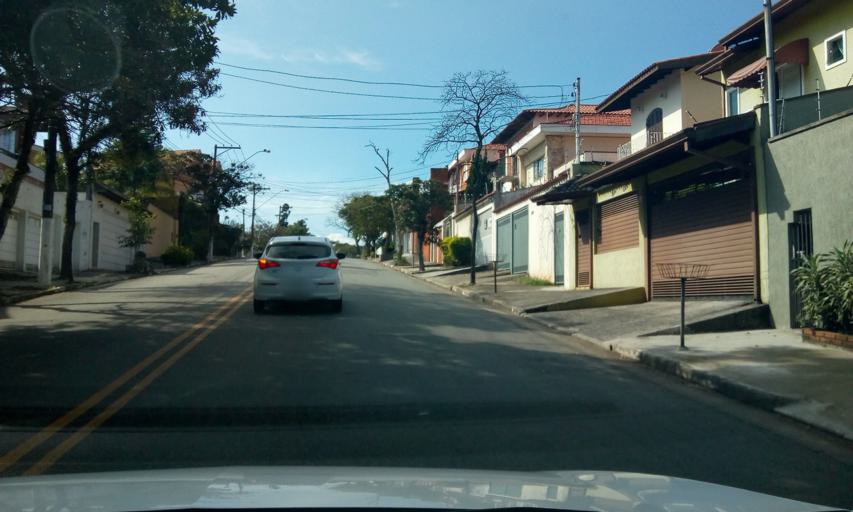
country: BR
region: Sao Paulo
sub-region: Osasco
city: Osasco
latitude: -23.5614
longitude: -46.7707
